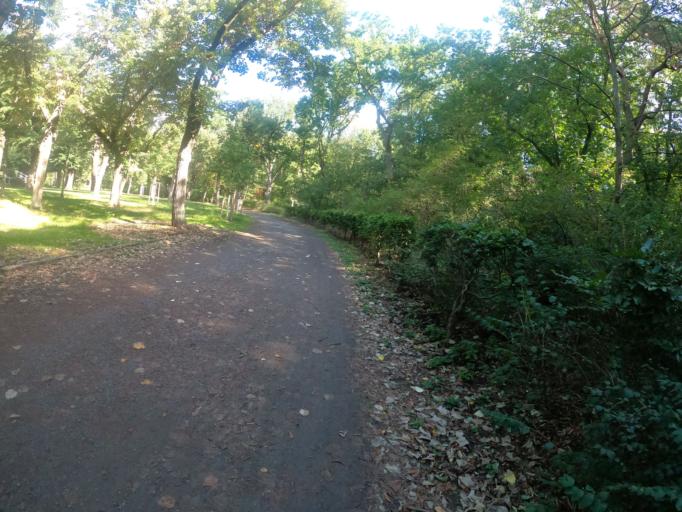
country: DE
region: Berlin
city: Charlottenburg-Nord
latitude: 52.5435
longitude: 13.2919
